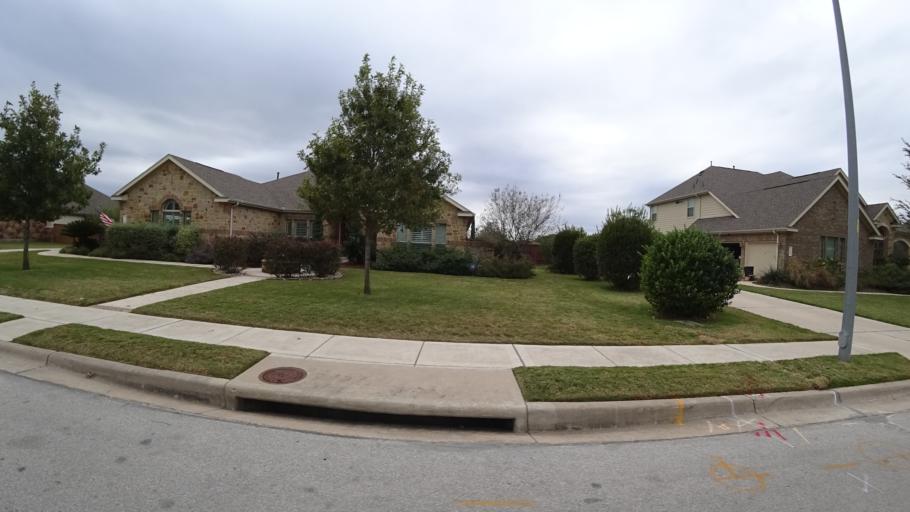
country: US
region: Texas
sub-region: Travis County
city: Shady Hollow
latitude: 30.1446
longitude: -97.8547
